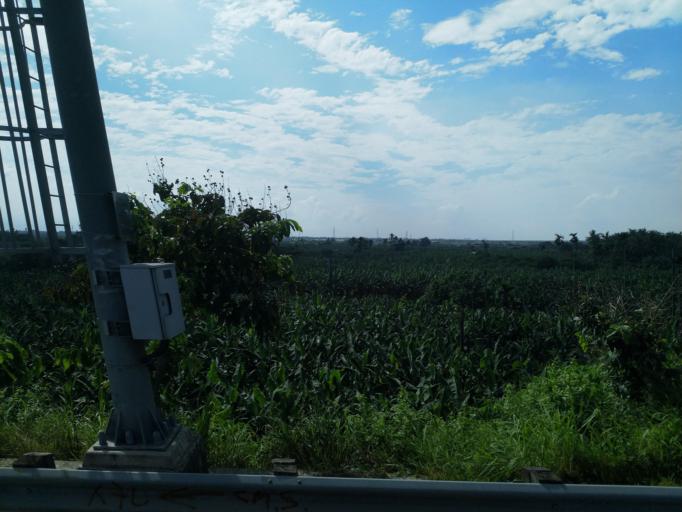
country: TW
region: Taiwan
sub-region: Pingtung
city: Pingtung
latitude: 22.7978
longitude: 120.4685
